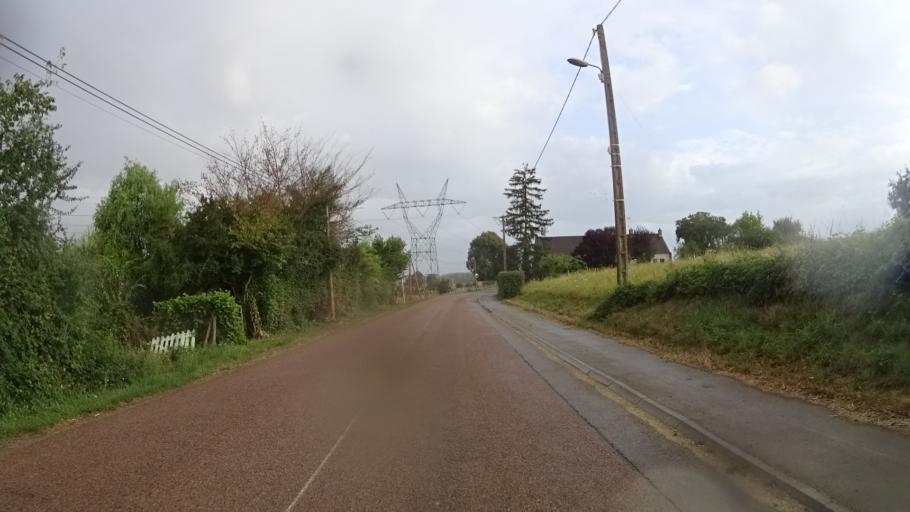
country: FR
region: Bourgogne
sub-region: Departement de Saone-et-Loire
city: Verdun-sur-le-Doubs
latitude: 46.9622
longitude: 5.0248
